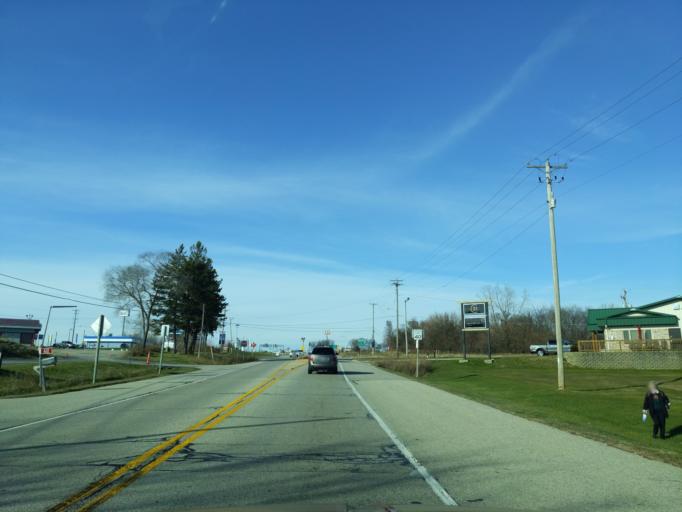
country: US
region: Wisconsin
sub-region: Rock County
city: Edgerton
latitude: 42.8320
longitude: -89.0227
